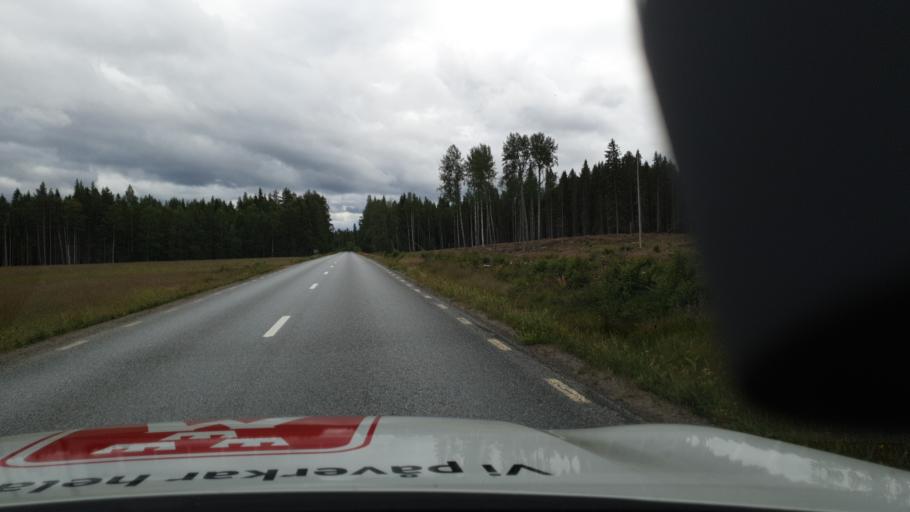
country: SE
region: Vaesterbotten
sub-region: Skelleftea Kommun
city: Burtraesk
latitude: 64.4446
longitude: 20.3958
